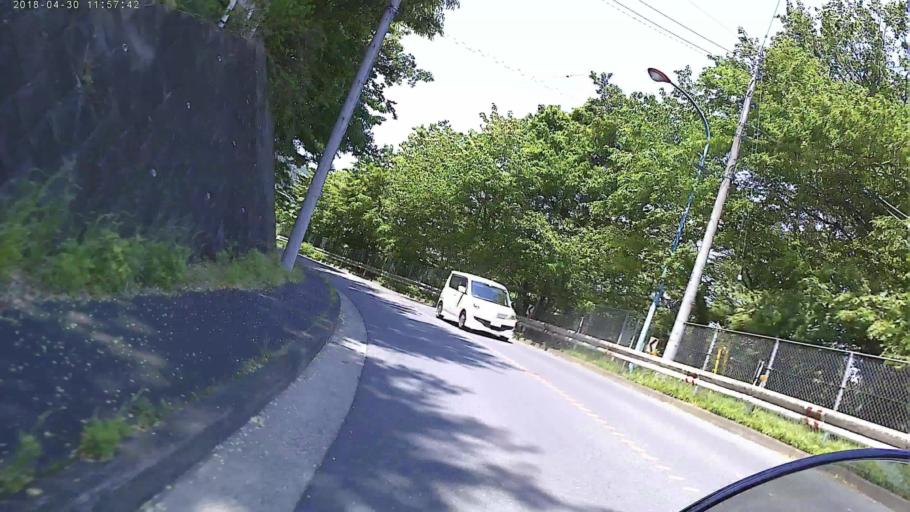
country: JP
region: Kanagawa
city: Zama
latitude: 35.4975
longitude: 139.3414
